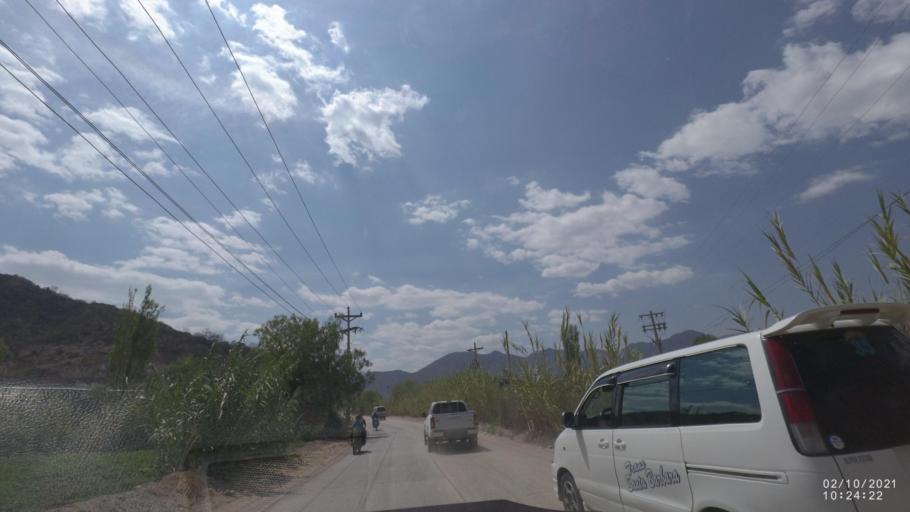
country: BO
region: Cochabamba
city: Irpa Irpa
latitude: -17.7252
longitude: -66.2754
